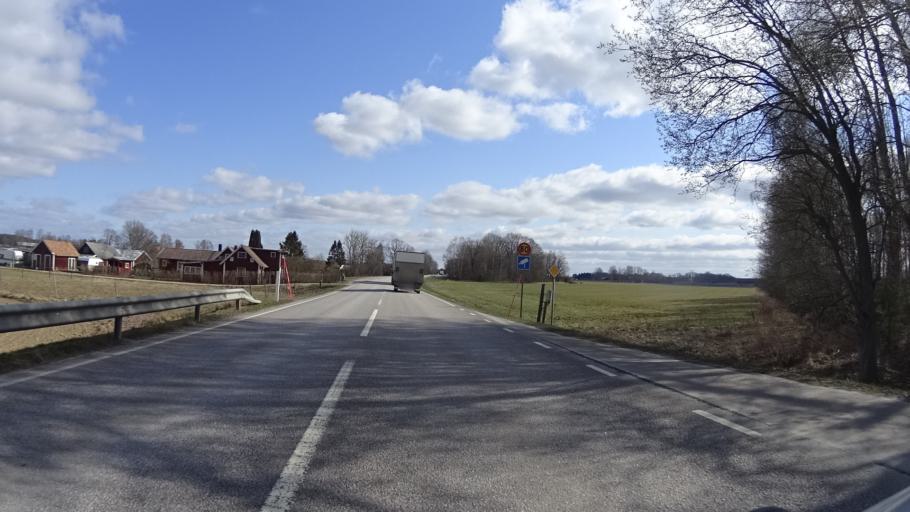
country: SE
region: OEstergoetland
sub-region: Mjolby Kommun
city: Mantorp
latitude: 58.3755
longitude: 15.2243
